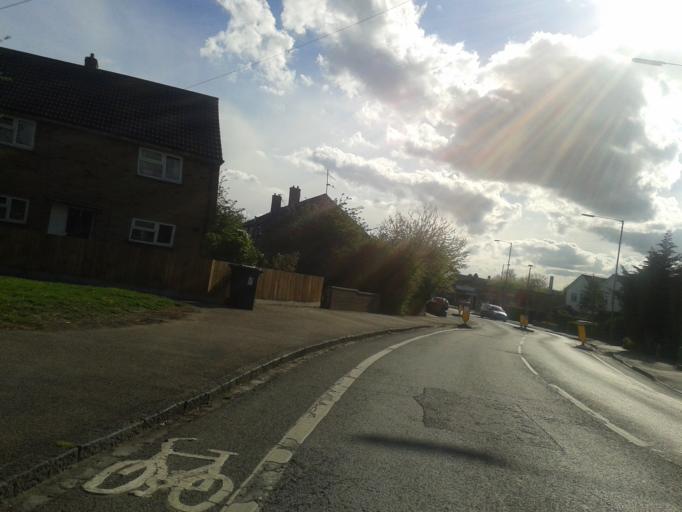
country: GB
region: England
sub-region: Cambridgeshire
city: Fulbourn
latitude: 52.1886
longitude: 0.1754
